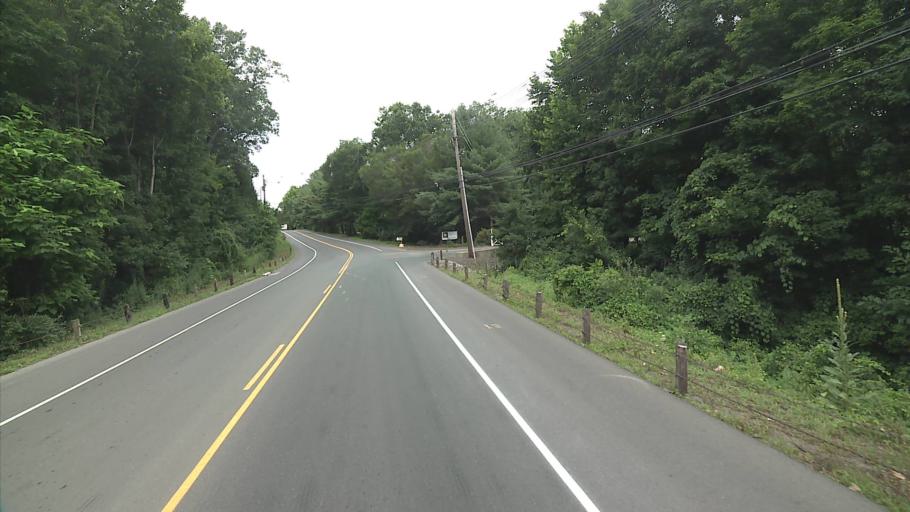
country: US
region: Connecticut
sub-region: New Haven County
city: Southbury
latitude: 41.5011
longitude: -73.2208
